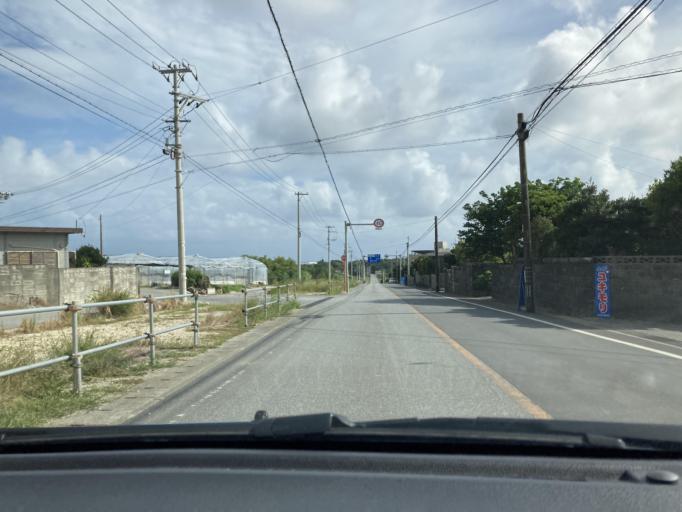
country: JP
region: Okinawa
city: Itoman
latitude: 26.1041
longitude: 127.6958
